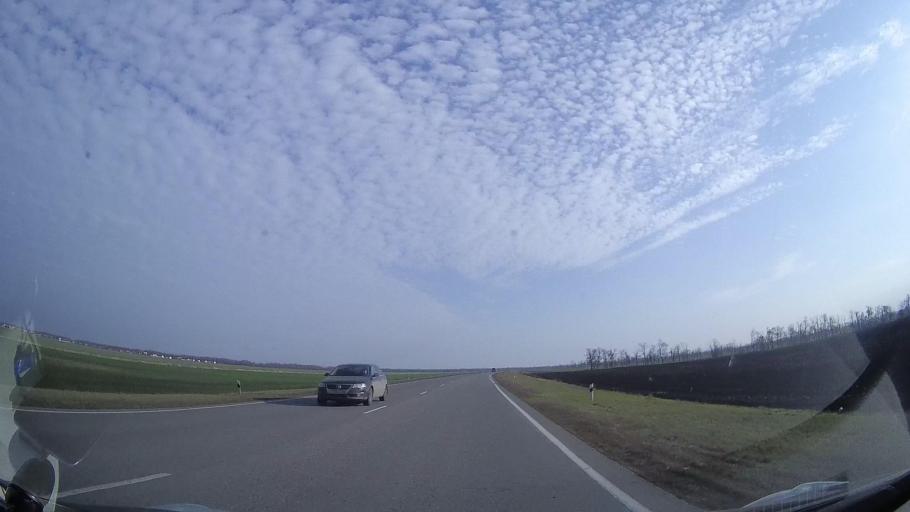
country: RU
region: Rostov
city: Tselina
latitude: 46.5140
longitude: 41.0405
